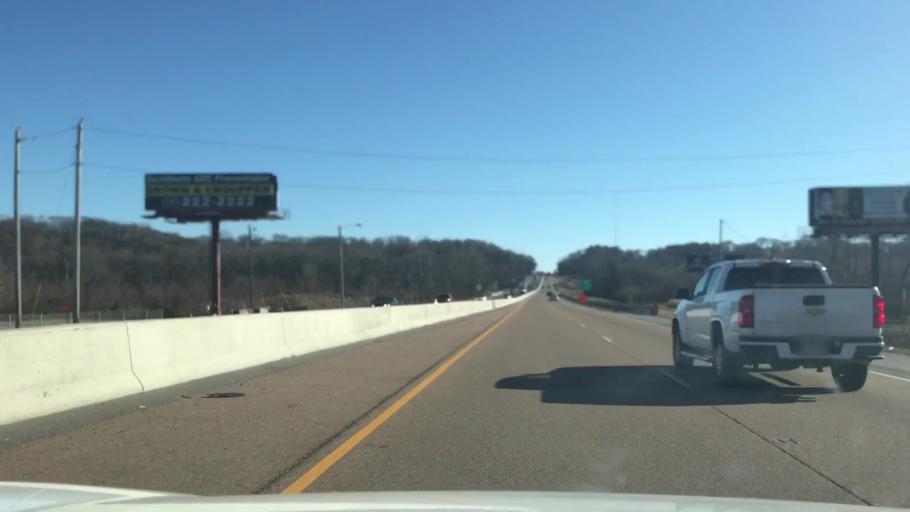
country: US
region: Illinois
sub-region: Saint Clair County
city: Alorton
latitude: 38.5718
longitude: -90.0961
